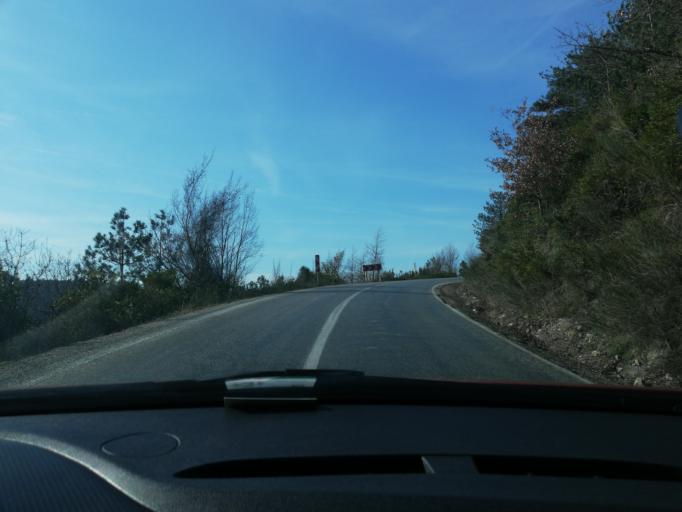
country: TR
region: Bartin
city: Kurucasile
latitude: 41.8462
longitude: 32.7590
